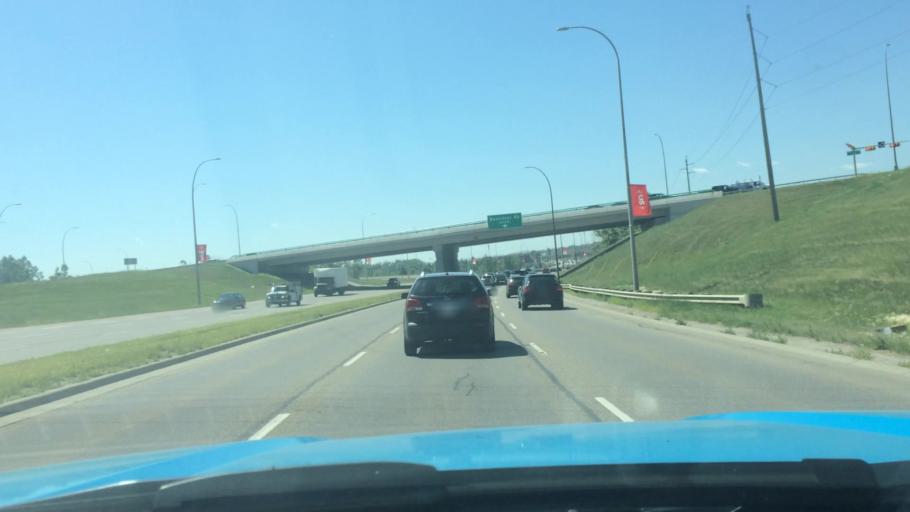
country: CA
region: Alberta
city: Calgary
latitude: 50.9328
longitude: -114.0686
